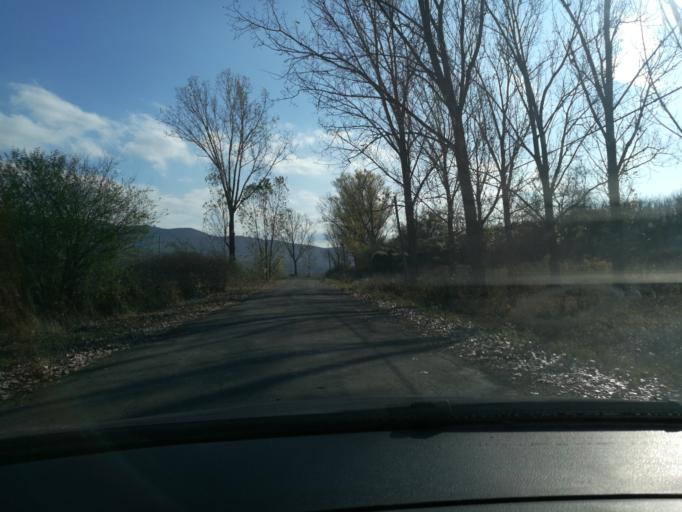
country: HU
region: Nograd
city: Paszto
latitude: 47.9020
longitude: 19.6888
